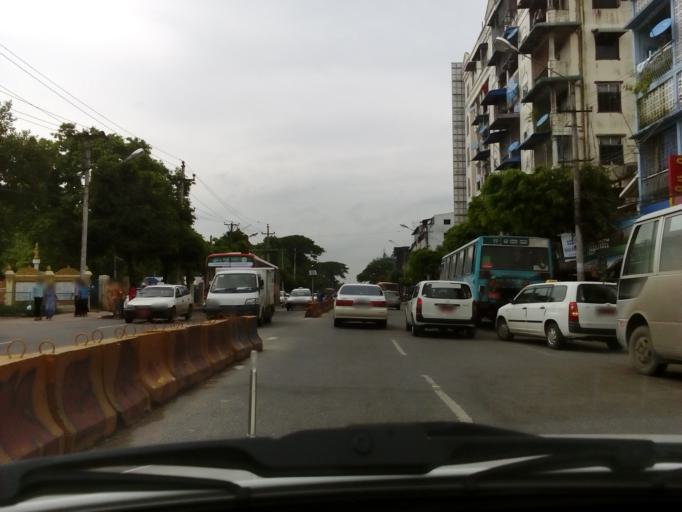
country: MM
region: Yangon
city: Yangon
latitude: 16.8568
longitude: 96.1566
